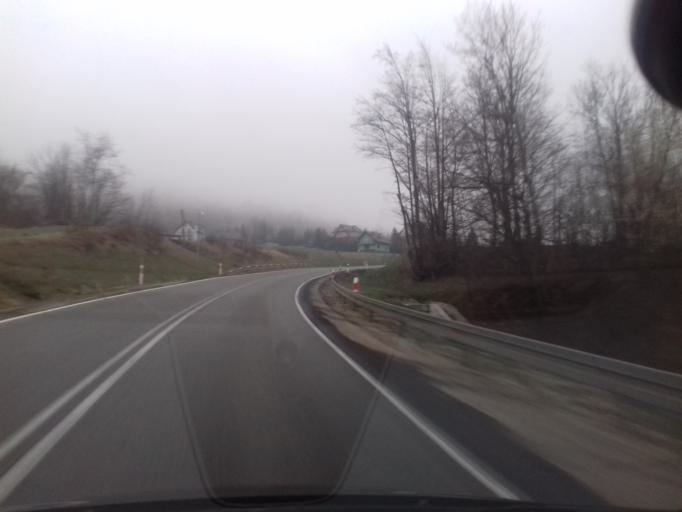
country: PL
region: Lesser Poland Voivodeship
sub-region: Powiat limanowski
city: Skrzydlna
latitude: 49.7004
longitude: 20.1895
